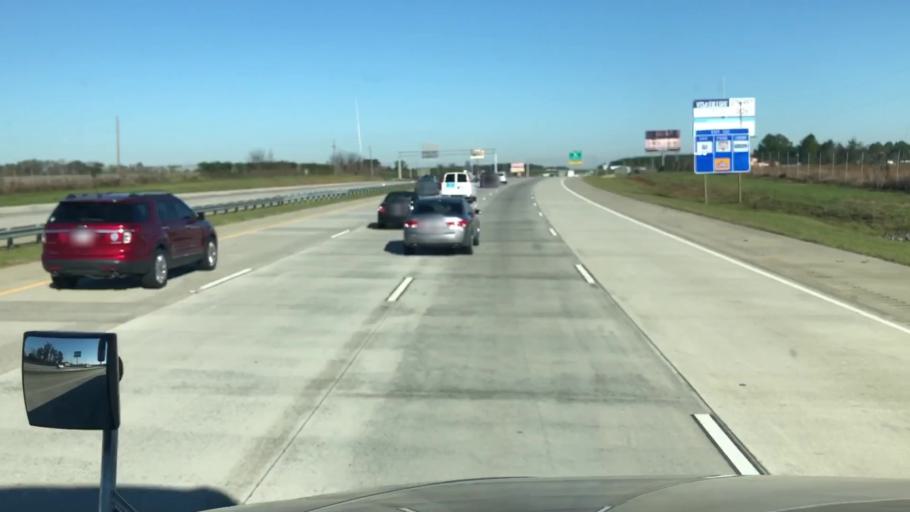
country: US
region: Georgia
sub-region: Dooly County
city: Unadilla
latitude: 32.2551
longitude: -83.7476
